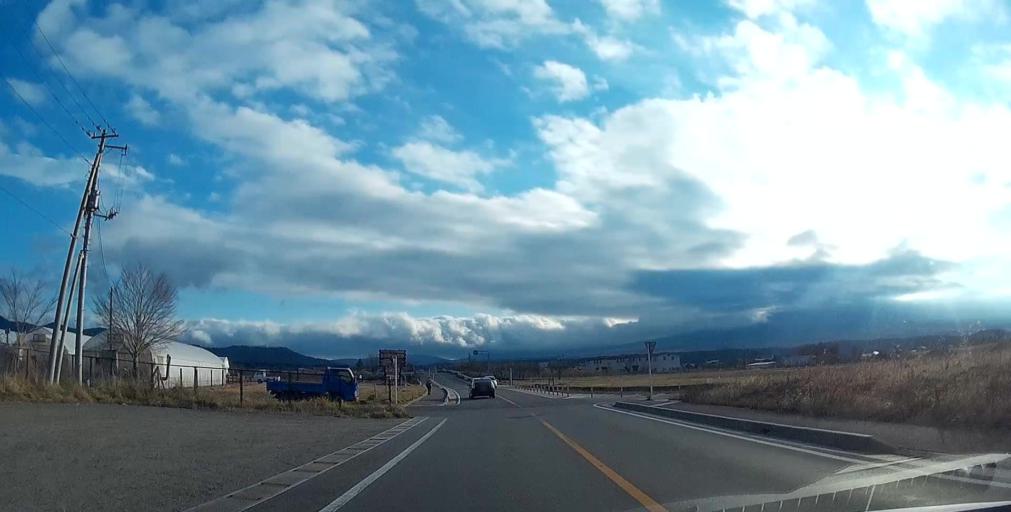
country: JP
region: Yamanashi
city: Fujikawaguchiko
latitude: 35.4658
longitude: 138.8420
